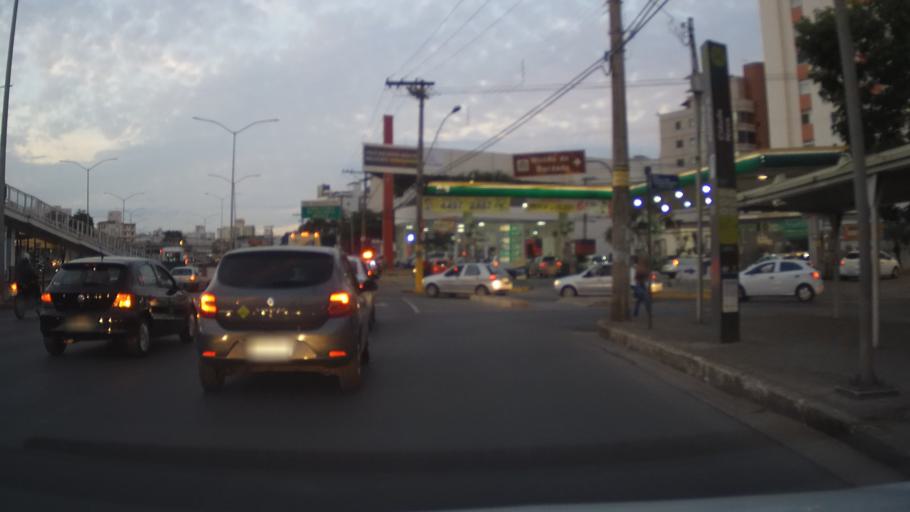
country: BR
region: Minas Gerais
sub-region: Belo Horizonte
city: Belo Horizonte
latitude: -19.8856
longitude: -43.9291
